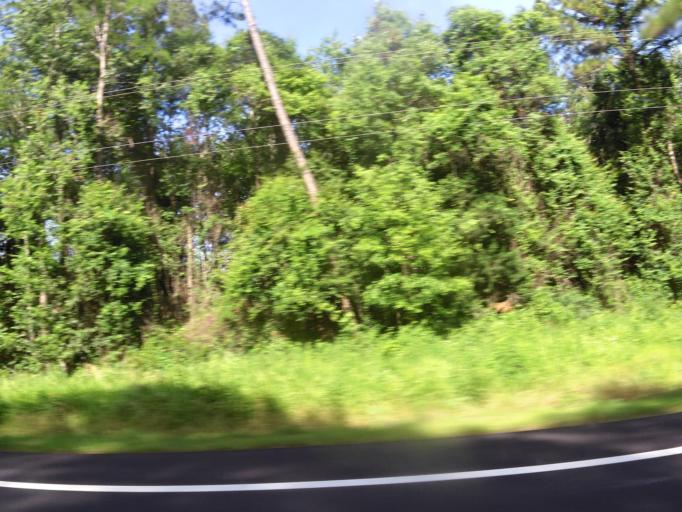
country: US
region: Florida
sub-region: Nassau County
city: Hilliard
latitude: 30.6482
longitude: -81.9030
